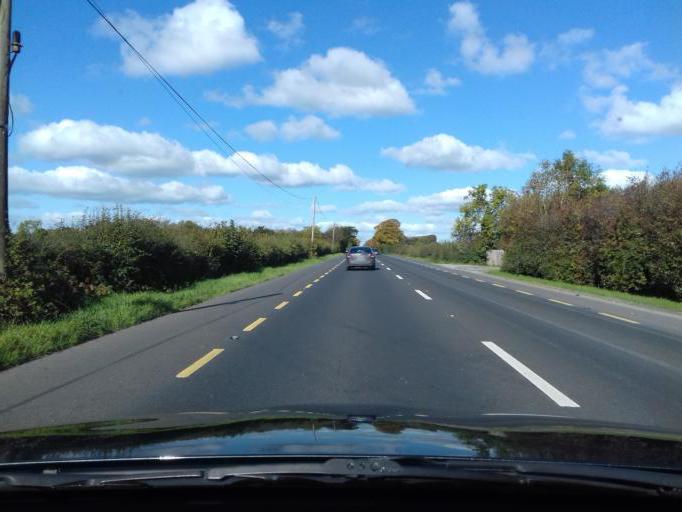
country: IE
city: Kentstown
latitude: 53.5915
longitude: -6.4638
